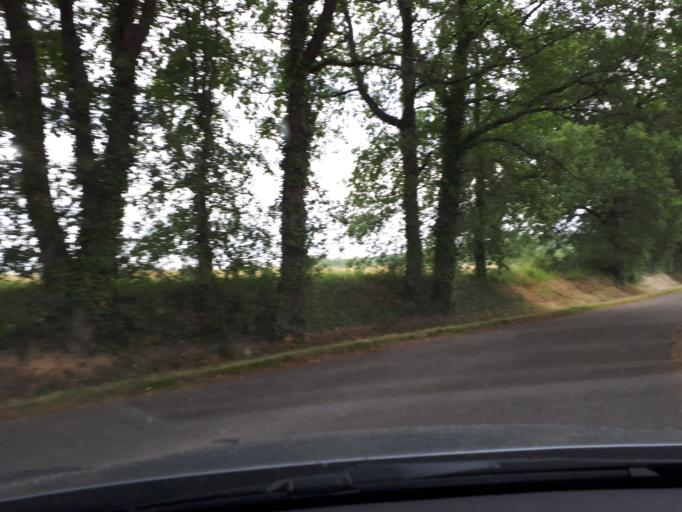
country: FR
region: Midi-Pyrenees
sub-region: Departement du Tarn-et-Garonne
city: Campsas
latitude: 43.8638
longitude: 1.3432
